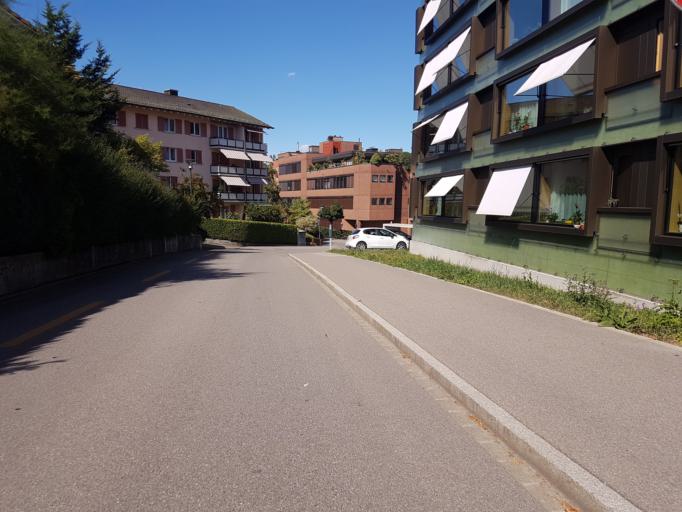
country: CH
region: Zurich
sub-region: Bezirk Pfaeffikon
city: Effretikon
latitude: 47.4272
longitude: 8.6846
